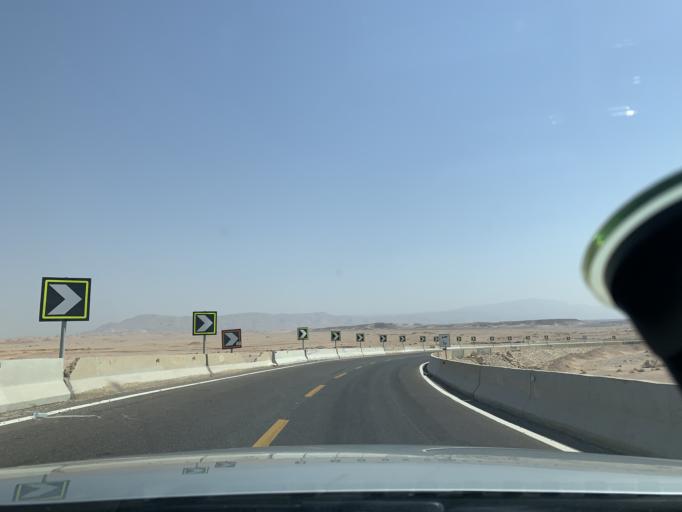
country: EG
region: As Suways
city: Ain Sukhna
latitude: 29.1071
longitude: 32.5338
